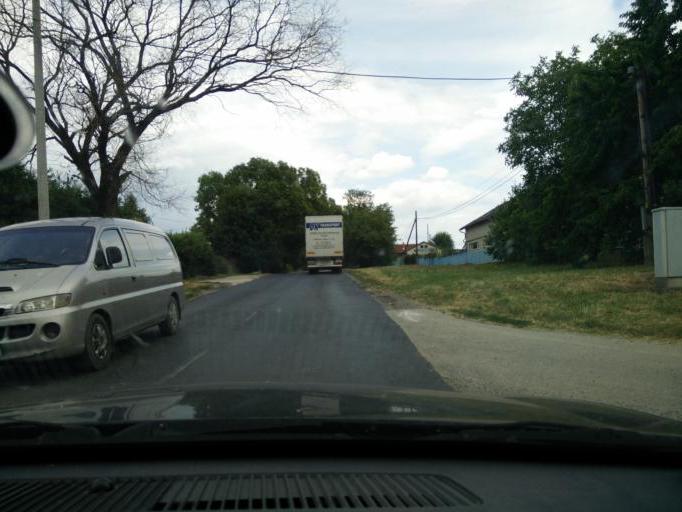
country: HU
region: Komarom-Esztergom
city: Tata
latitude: 47.6576
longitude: 18.3405
